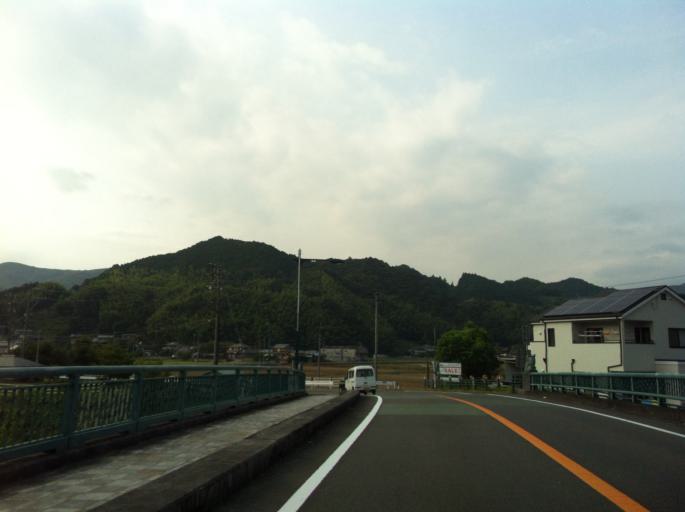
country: JP
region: Shizuoka
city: Fujieda
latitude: 34.9473
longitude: 138.2587
